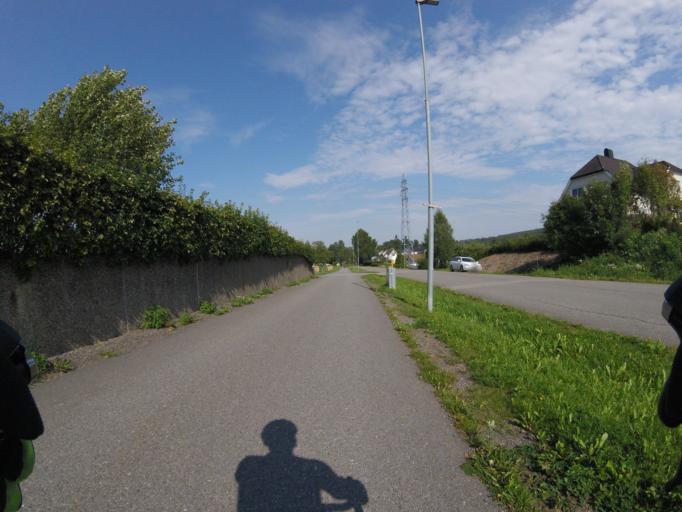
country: NO
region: Akershus
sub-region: Skedsmo
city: Leirsund
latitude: 59.9949
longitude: 11.0836
